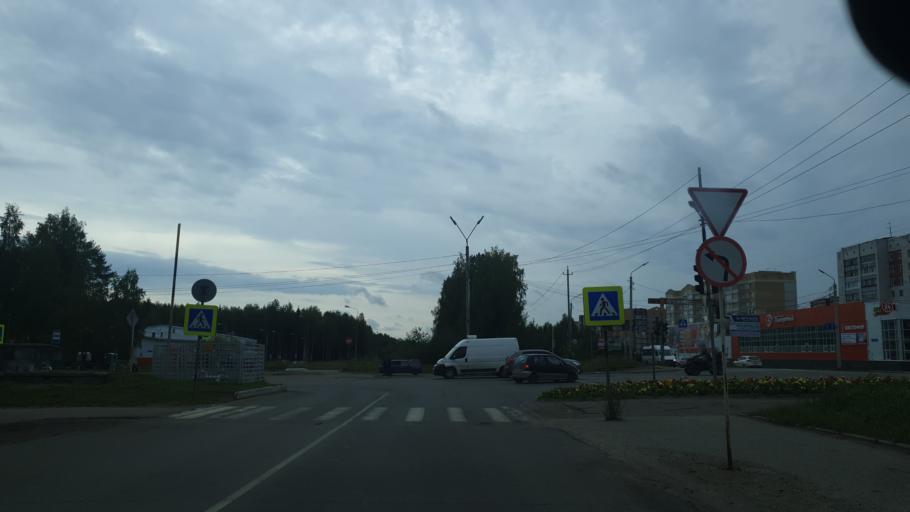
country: RU
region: Komi Republic
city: Ezhva
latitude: 61.7818
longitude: 50.7483
